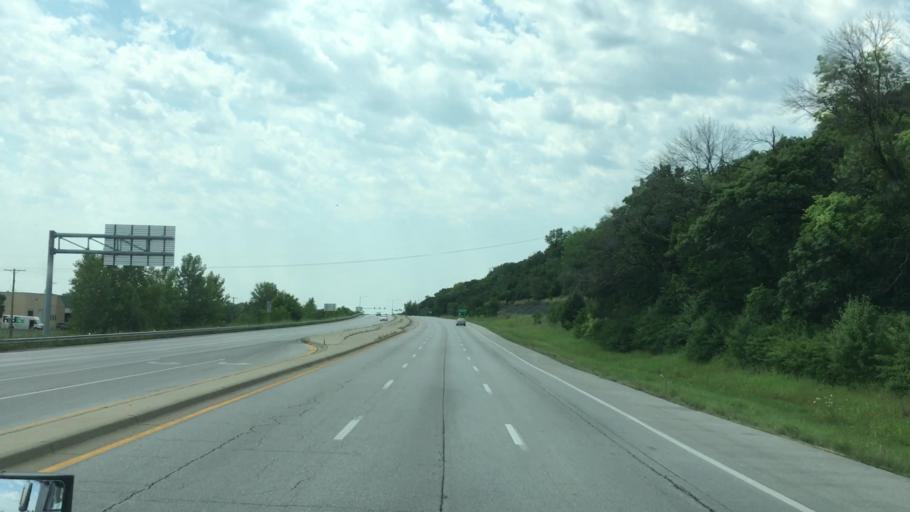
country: US
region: Missouri
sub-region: Platte County
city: Riverside
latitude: 39.1739
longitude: -94.6322
